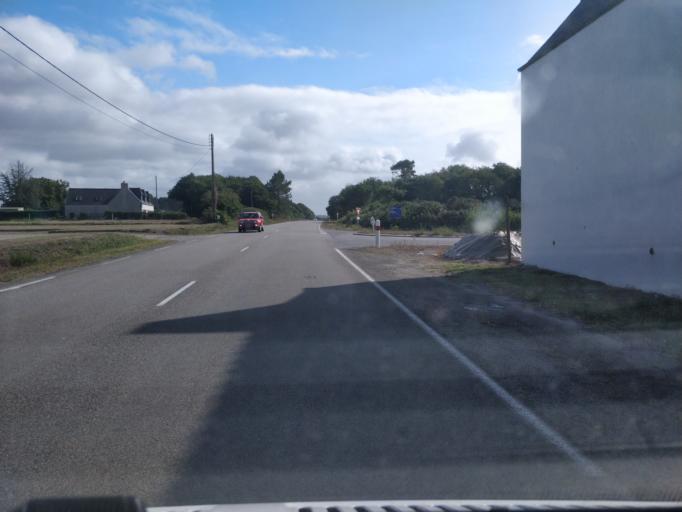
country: FR
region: Brittany
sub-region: Departement du Finistere
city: Plozevet
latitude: 47.9948
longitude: -4.3944
